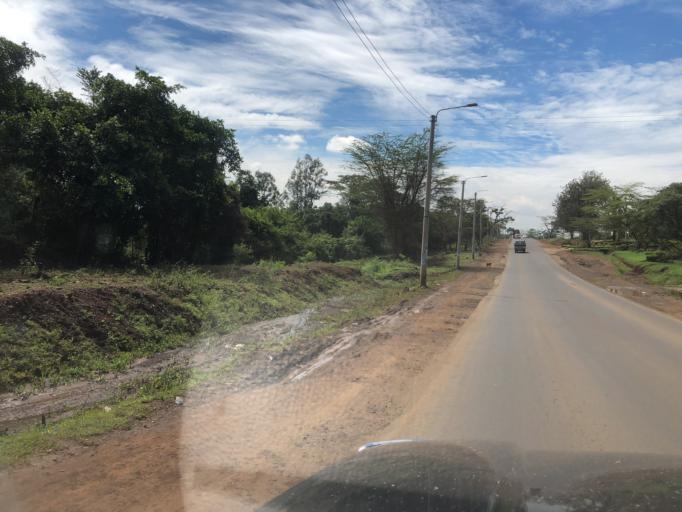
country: KE
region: Nairobi Area
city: Nairobi
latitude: -1.3646
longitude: 36.7661
